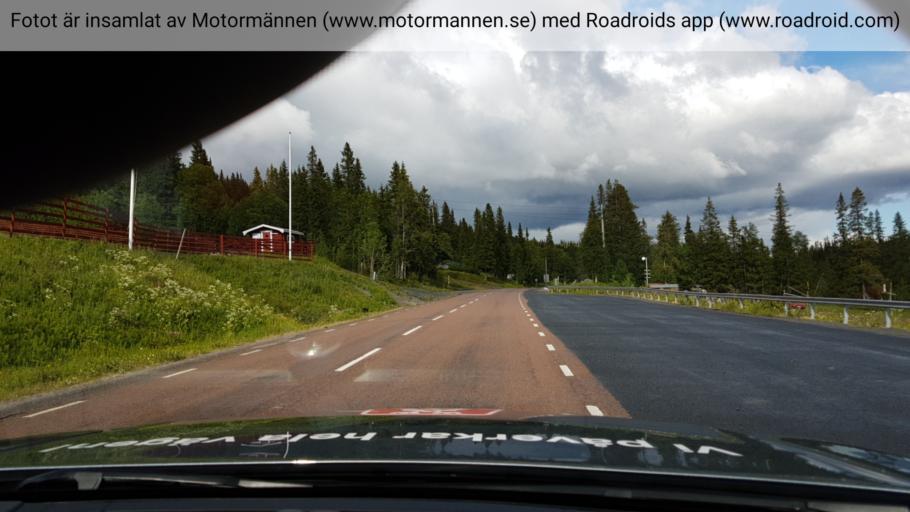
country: SE
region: Jaemtland
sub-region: Are Kommun
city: Jarpen
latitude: 63.1027
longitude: 13.8014
